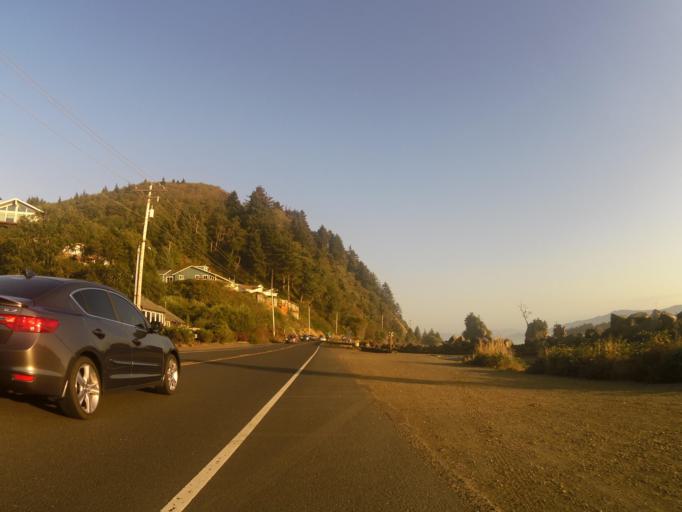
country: US
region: Oregon
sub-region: Tillamook County
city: Rockaway Beach
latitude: 45.5644
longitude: -123.9368
